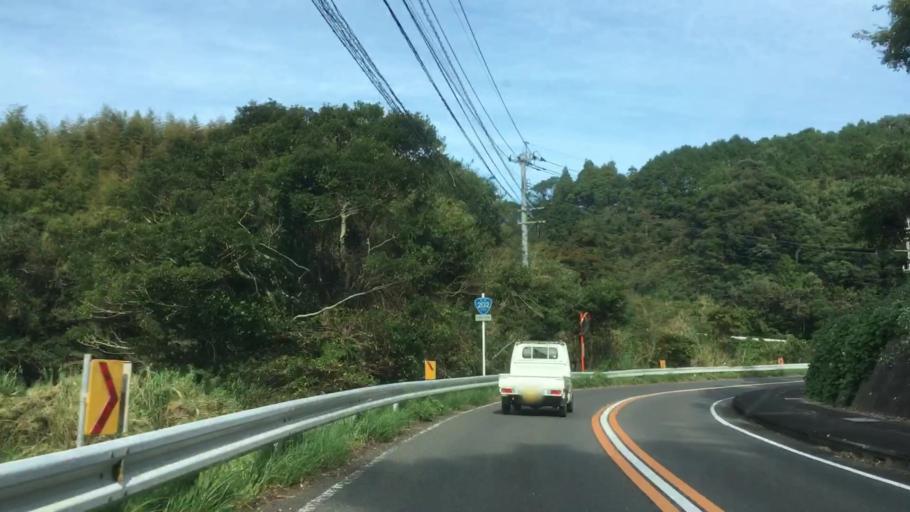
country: JP
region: Nagasaki
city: Sasebo
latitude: 33.0254
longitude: 129.6535
